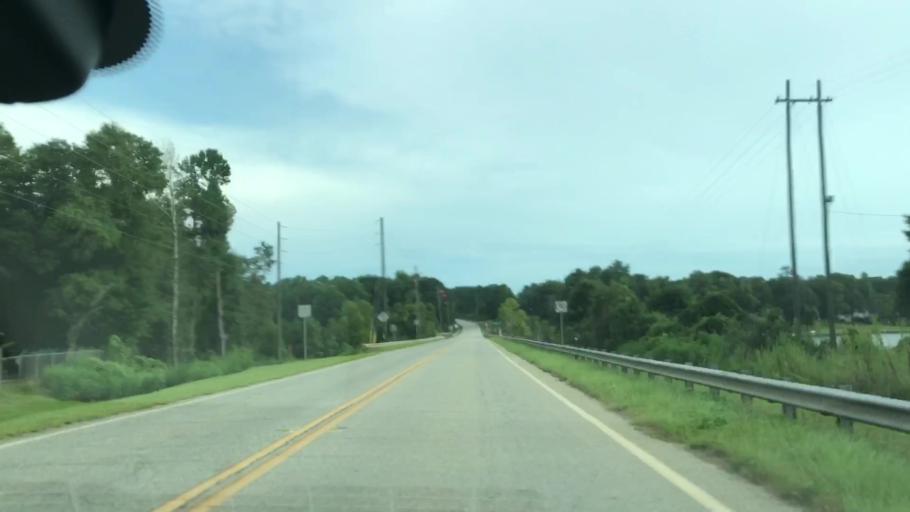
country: US
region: Georgia
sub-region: Clay County
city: Fort Gaines
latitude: 31.7503
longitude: -85.0551
